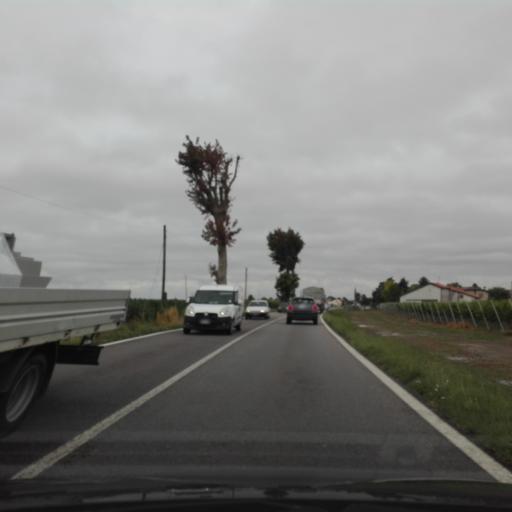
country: IT
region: Veneto
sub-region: Provincia di Rovigo
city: Villanova del Ghebbo Canton
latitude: 45.0758
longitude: 11.6377
